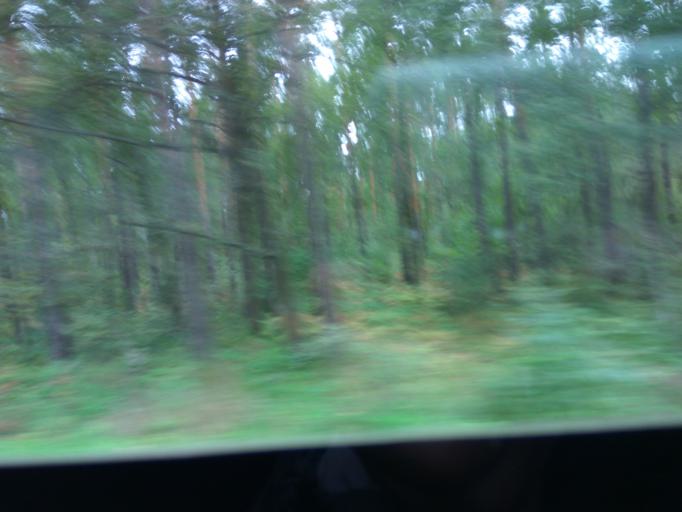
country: RU
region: Moskovskaya
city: Malyshevo
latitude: 55.5235
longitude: 38.3439
